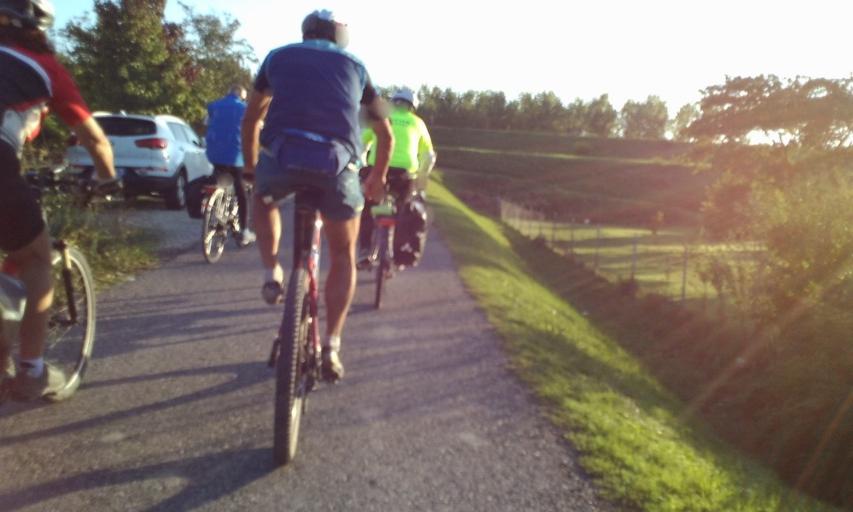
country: IT
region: Lombardy
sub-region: Provincia di Mantova
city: Ostiglia
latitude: 45.0754
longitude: 11.1213
